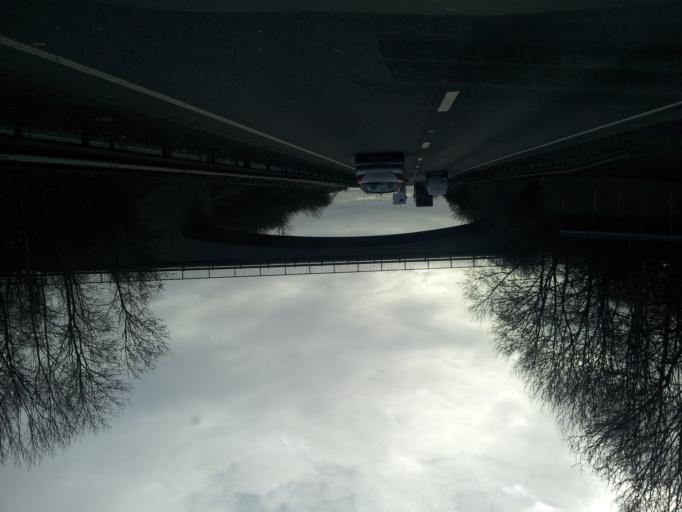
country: GB
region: England
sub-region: Lincolnshire
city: Grantham
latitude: 52.8926
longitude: -0.6497
